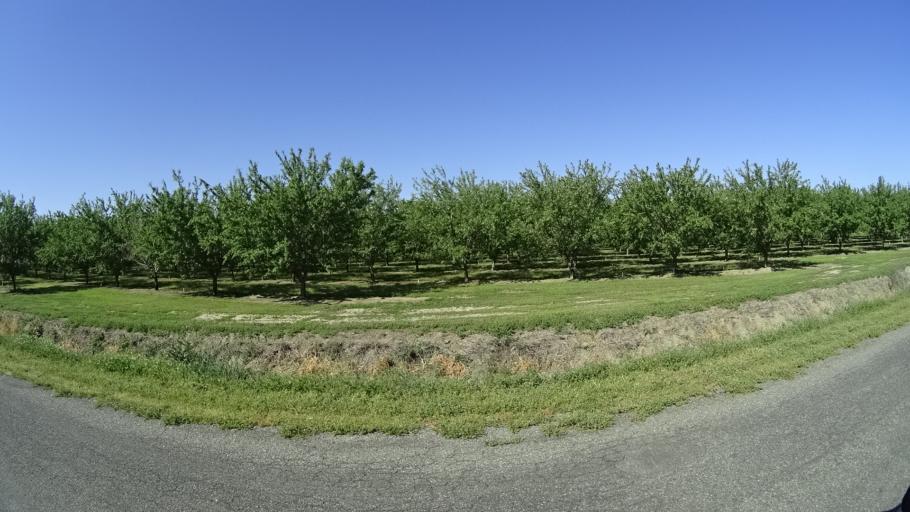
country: US
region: California
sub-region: Glenn County
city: Hamilton City
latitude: 39.7283
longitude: -122.0145
